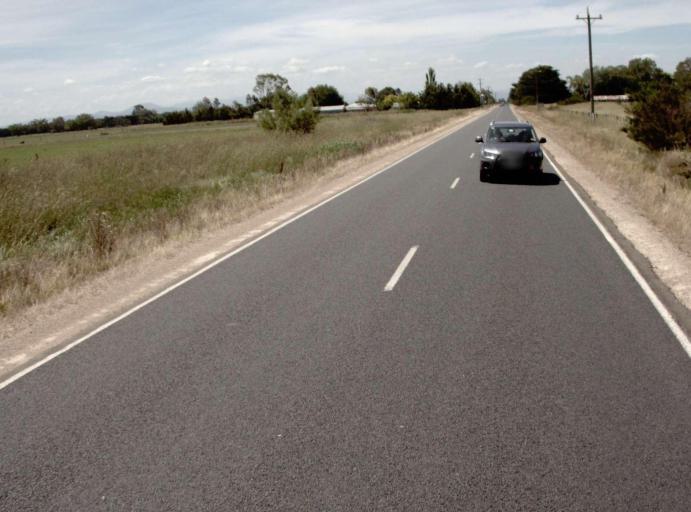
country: AU
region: Victoria
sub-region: Wellington
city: Heyfield
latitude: -38.0340
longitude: 146.8786
